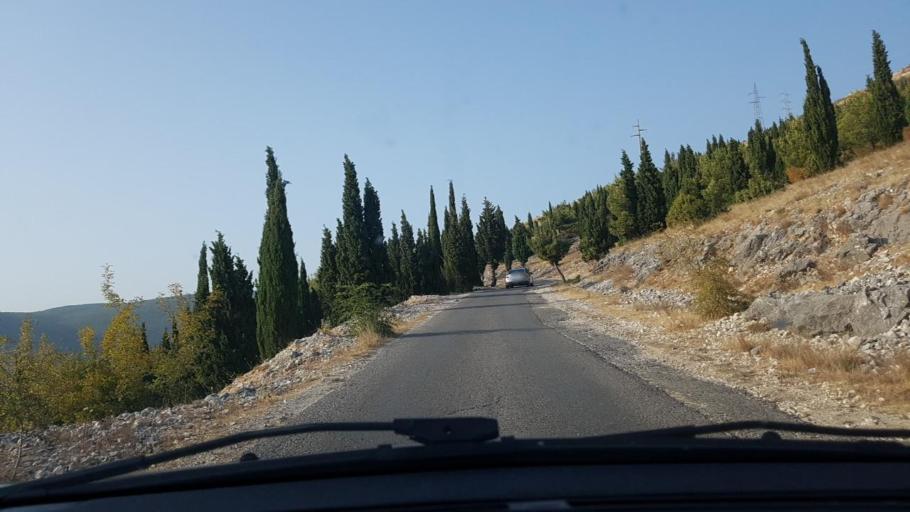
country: BA
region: Federation of Bosnia and Herzegovina
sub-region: Hercegovacko-Bosanski Kanton
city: Mostar
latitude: 43.3501
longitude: 17.8223
